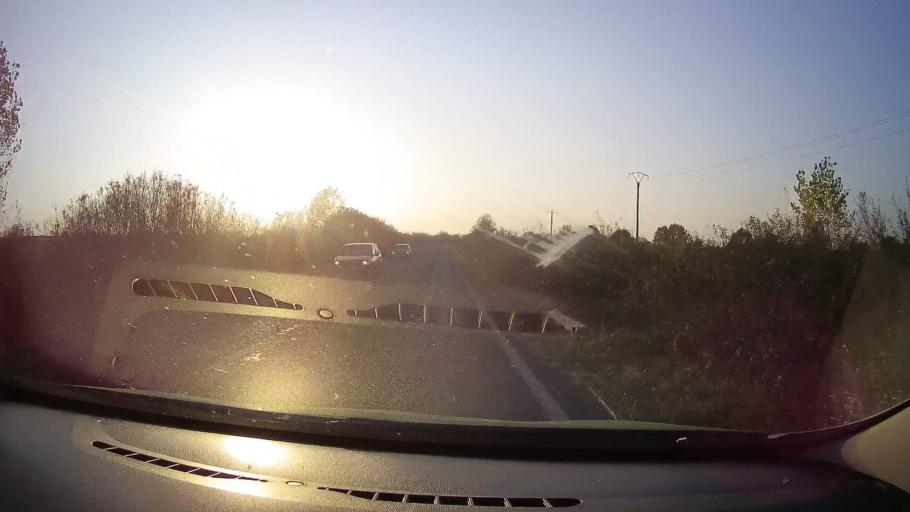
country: RO
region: Arad
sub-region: Comuna Barsa
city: Barsa
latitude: 46.3908
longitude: 22.0565
